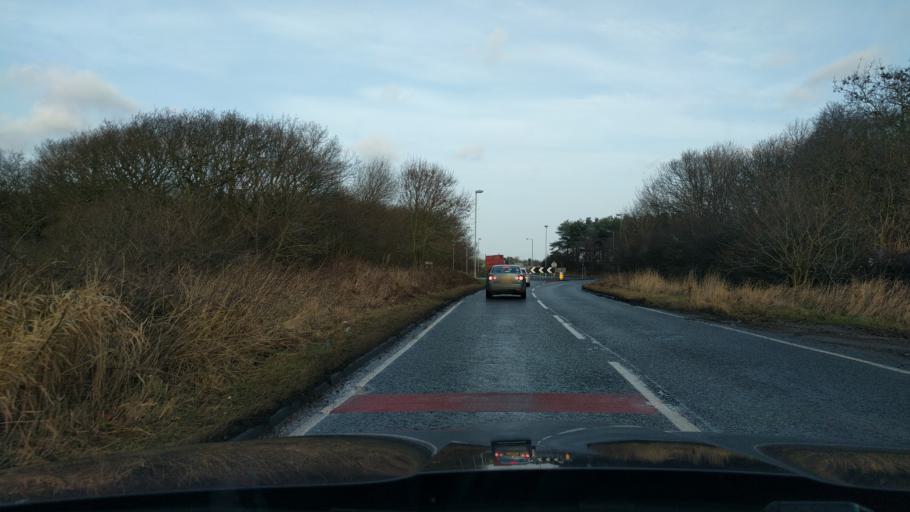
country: GB
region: England
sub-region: Northumberland
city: Cresswell
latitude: 55.2076
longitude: -1.5735
